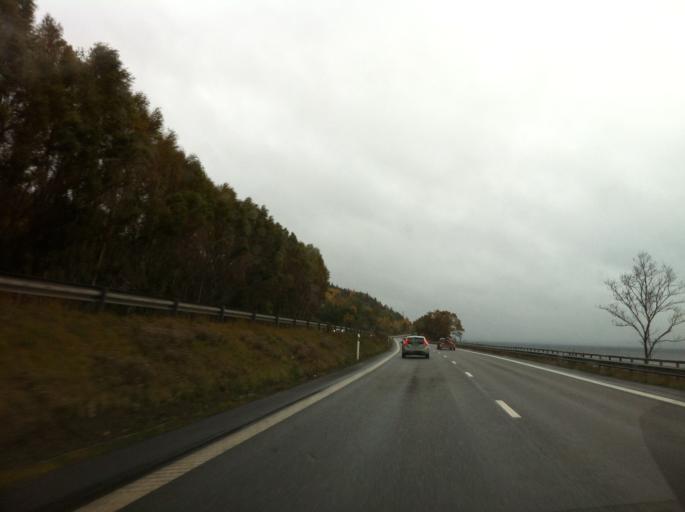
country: SE
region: Joenkoeping
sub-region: Jonkopings Kommun
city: Kaxholmen
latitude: 57.8800
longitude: 14.2782
